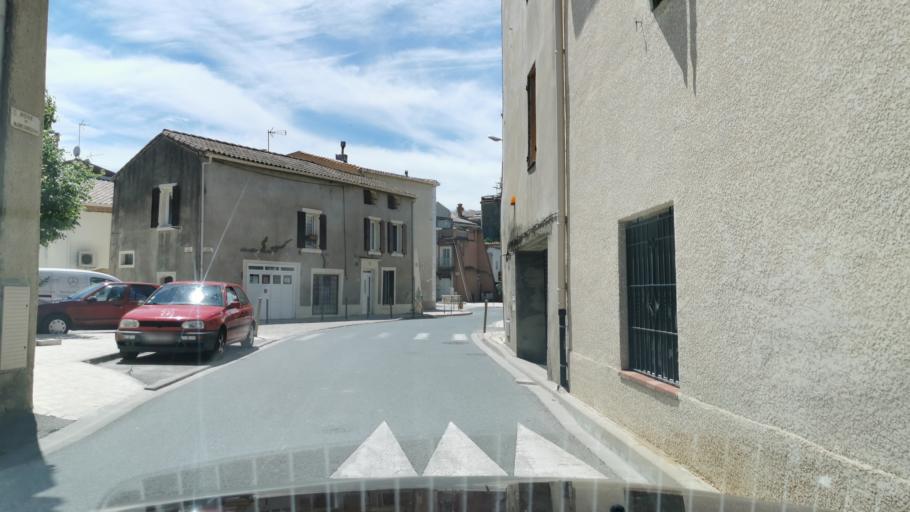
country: FR
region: Languedoc-Roussillon
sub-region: Departement de l'Aude
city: Nevian
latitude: 43.2126
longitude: 2.9046
